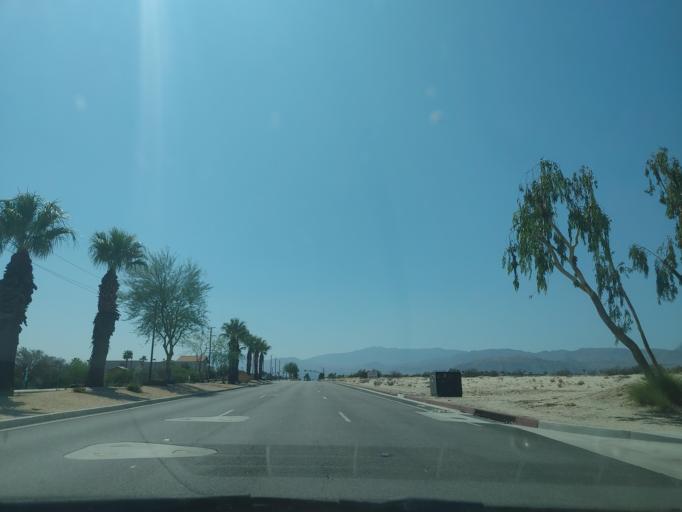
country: US
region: California
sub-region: Riverside County
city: Thousand Palms
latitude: 33.7983
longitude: -116.3883
